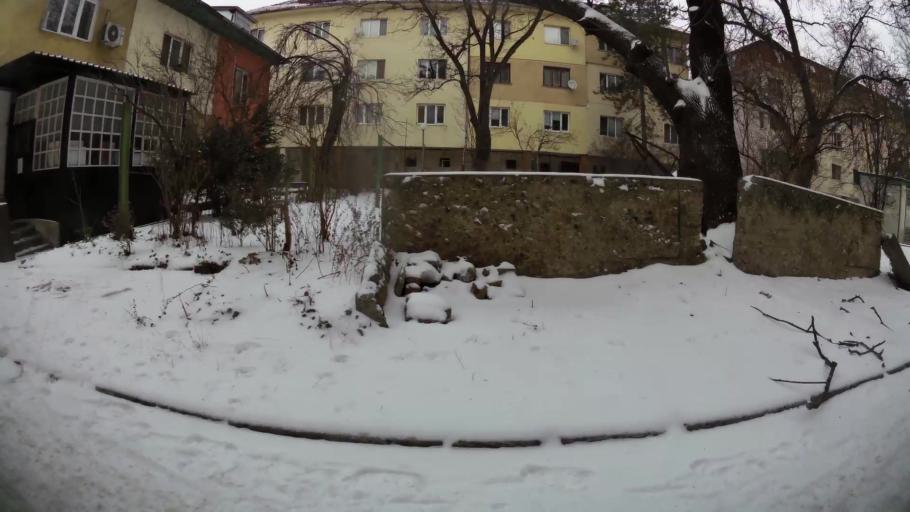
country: BG
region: Sofia-Capital
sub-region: Stolichna Obshtina
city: Sofia
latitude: 42.7151
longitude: 23.2888
